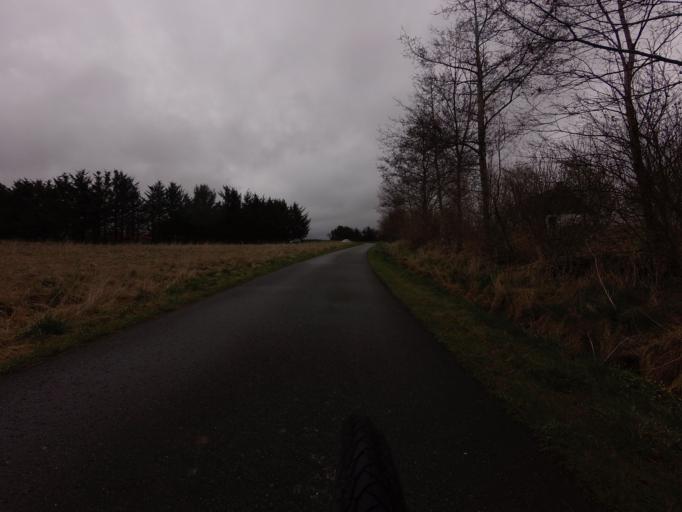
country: DK
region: North Denmark
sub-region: Jammerbugt Kommune
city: Pandrup
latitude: 57.3371
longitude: 9.7801
